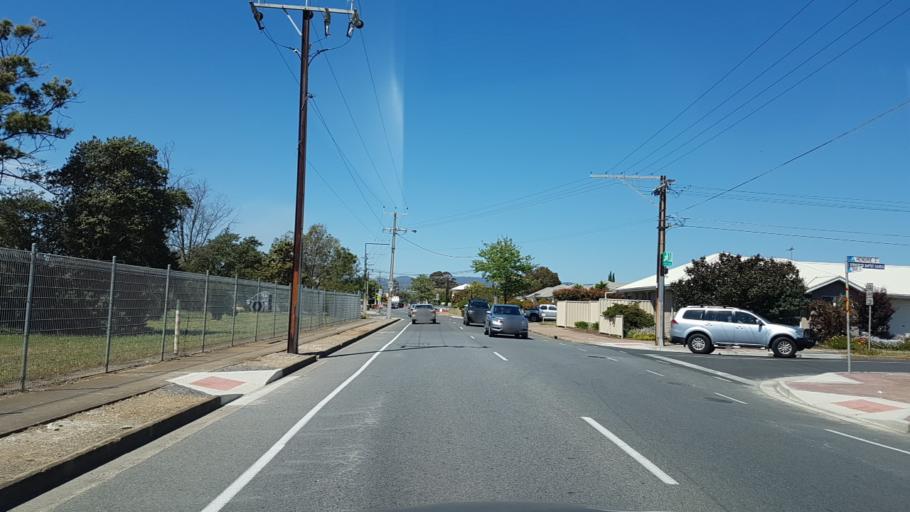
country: AU
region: South Australia
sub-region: Marion
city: Plympton Park
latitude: -34.9809
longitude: 138.5462
